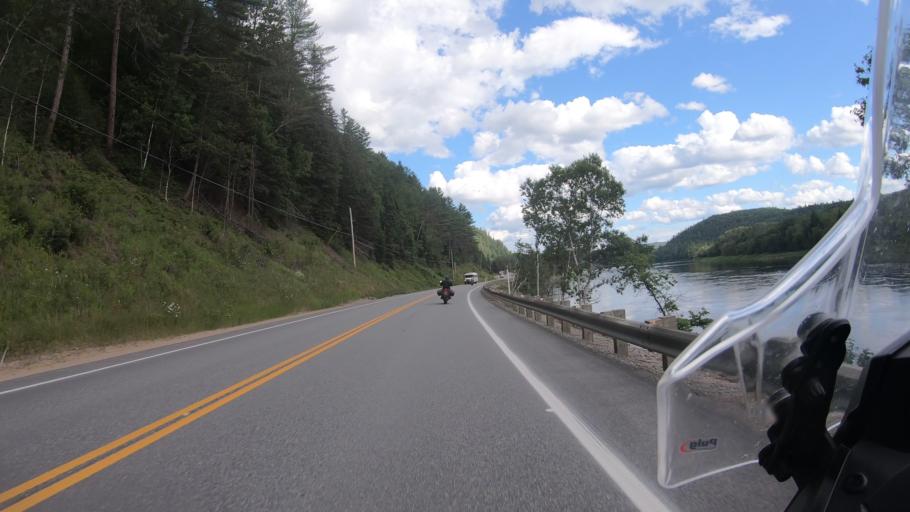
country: CA
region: Quebec
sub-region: Mauricie
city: Saint-Tite
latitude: 46.9954
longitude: -72.9183
